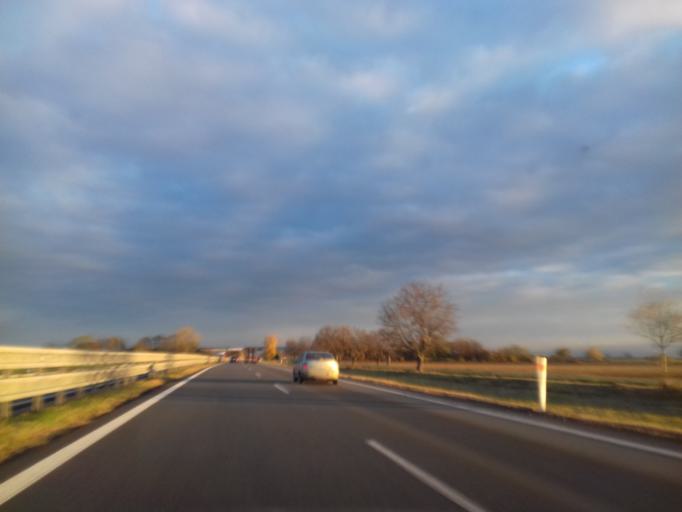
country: CZ
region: Olomoucky
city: Urcice
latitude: 49.4213
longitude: 17.1115
